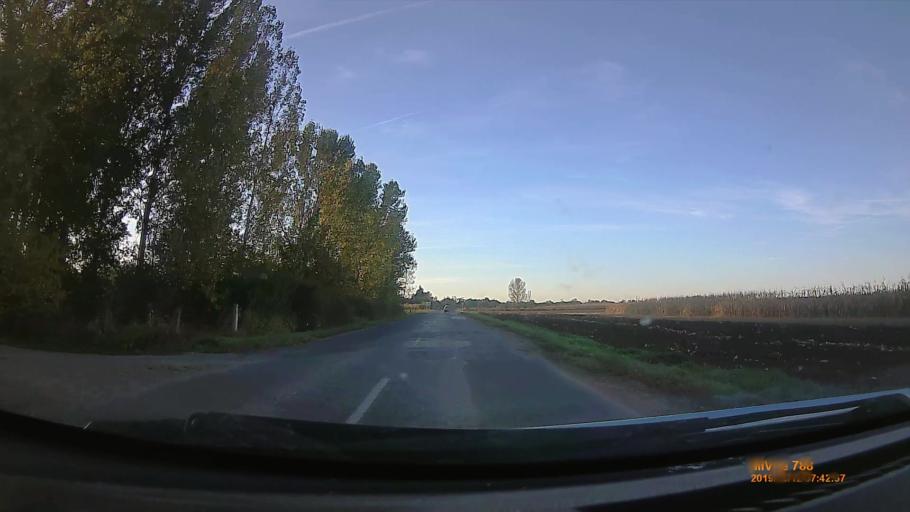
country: RO
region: Bihor
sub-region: Comuna Bors
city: Bors
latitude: 47.1975
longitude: 21.7885
